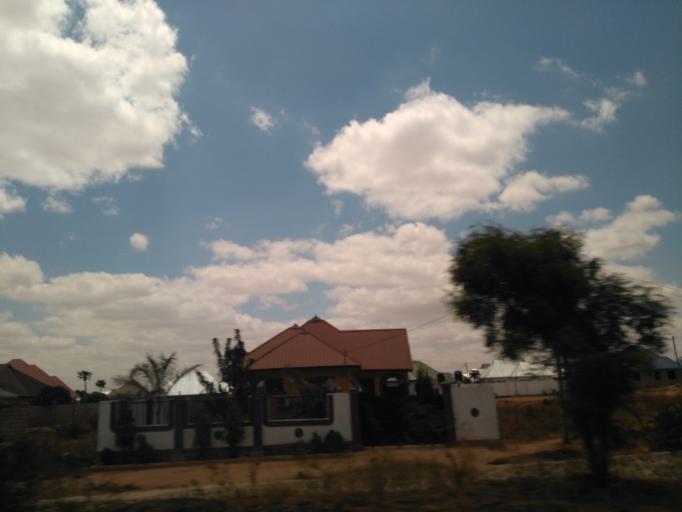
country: TZ
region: Dodoma
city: Kisasa
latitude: -6.1779
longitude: 35.7936
